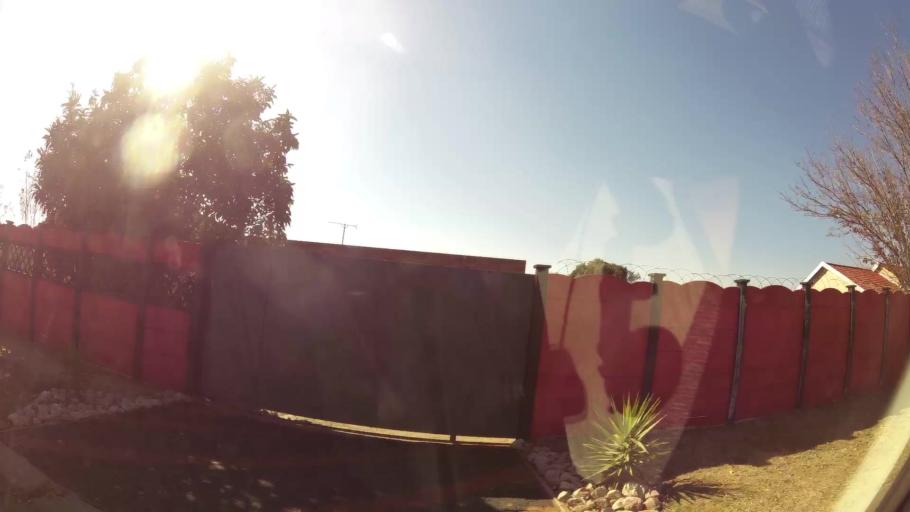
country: ZA
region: Gauteng
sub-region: City of Johannesburg Metropolitan Municipality
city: Johannesburg
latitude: -26.2533
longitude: 28.1015
